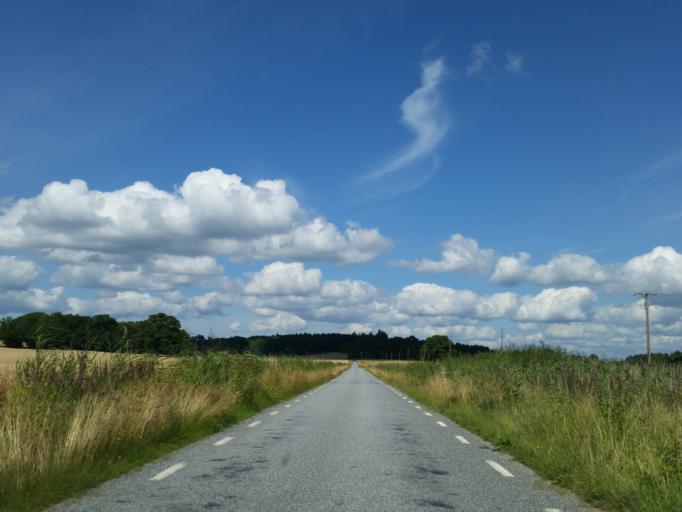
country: SE
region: Stockholm
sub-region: Sodertalje Kommun
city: Pershagen
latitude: 59.0441
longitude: 17.6586
